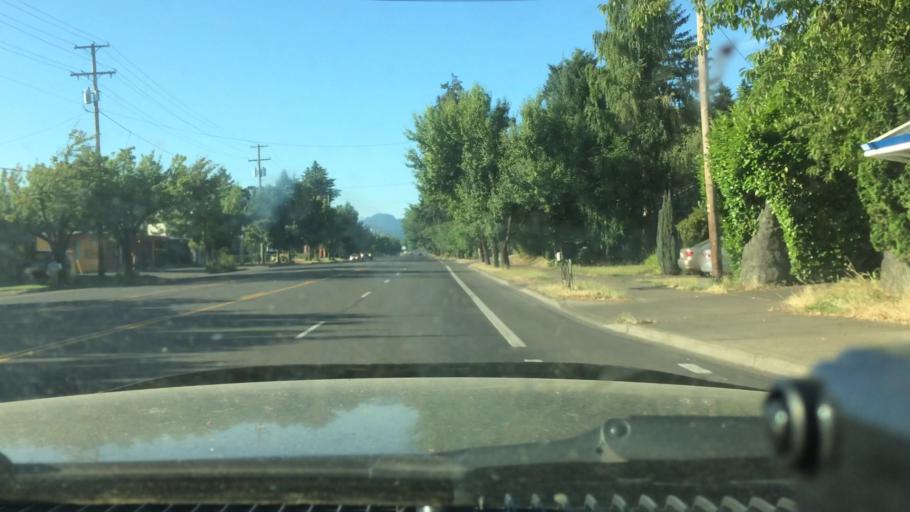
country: US
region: Oregon
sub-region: Lane County
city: Eugene
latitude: 44.0711
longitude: -123.1186
